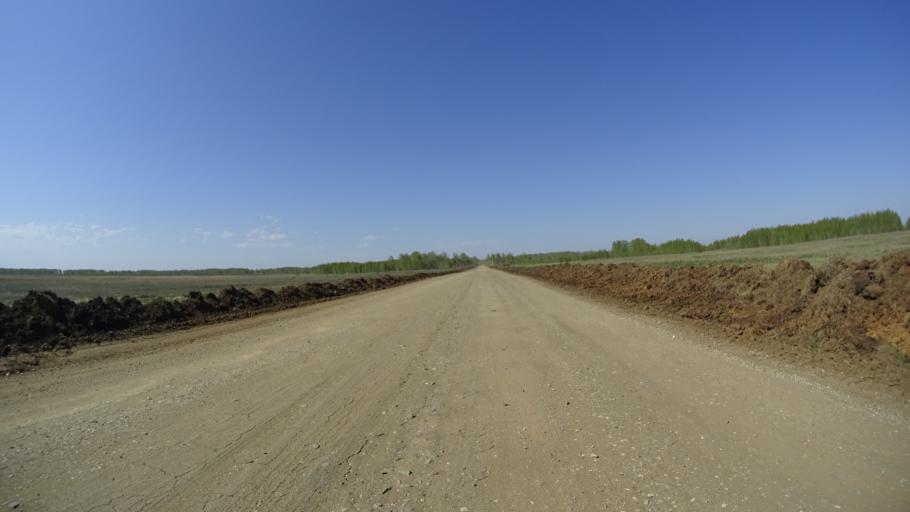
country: RU
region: Chelyabinsk
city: Troitsk
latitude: 54.1805
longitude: 61.4763
